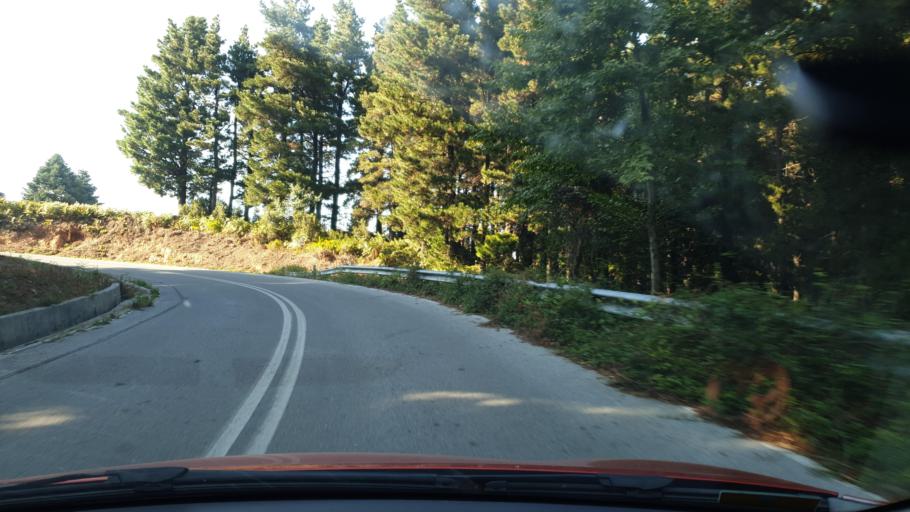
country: GR
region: Central Greece
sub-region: Nomos Evvoias
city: Kymi
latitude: 38.6330
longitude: 23.9329
